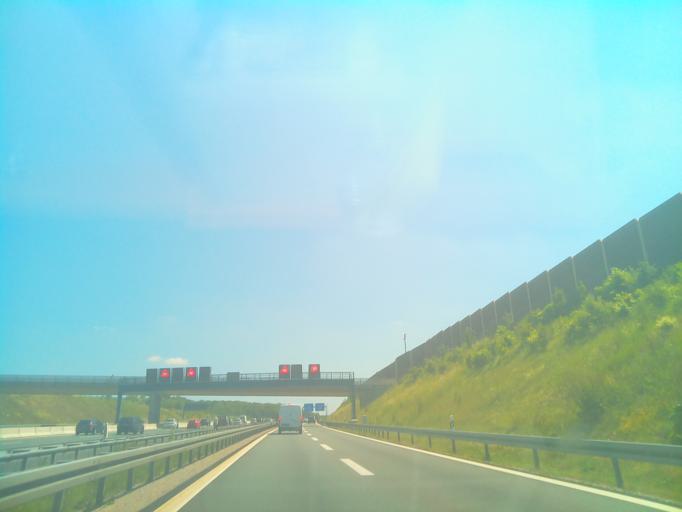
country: DE
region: Bavaria
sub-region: Regierungsbezirk Unterfranken
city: Eisingen
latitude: 49.7488
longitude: 9.8341
